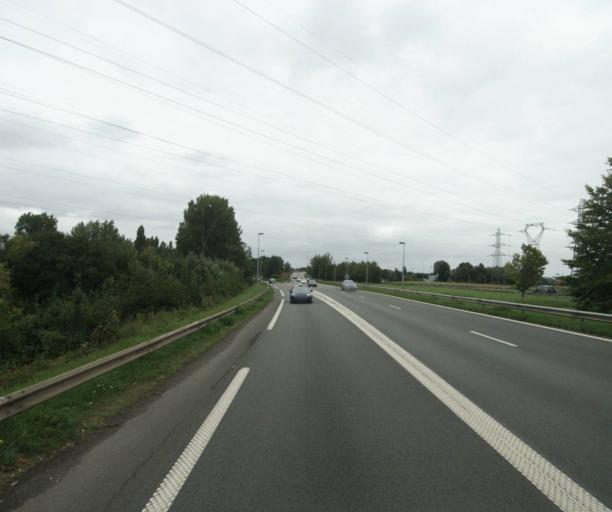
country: FR
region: Nord-Pas-de-Calais
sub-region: Departement du Nord
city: Hem
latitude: 50.6482
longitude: 3.1650
